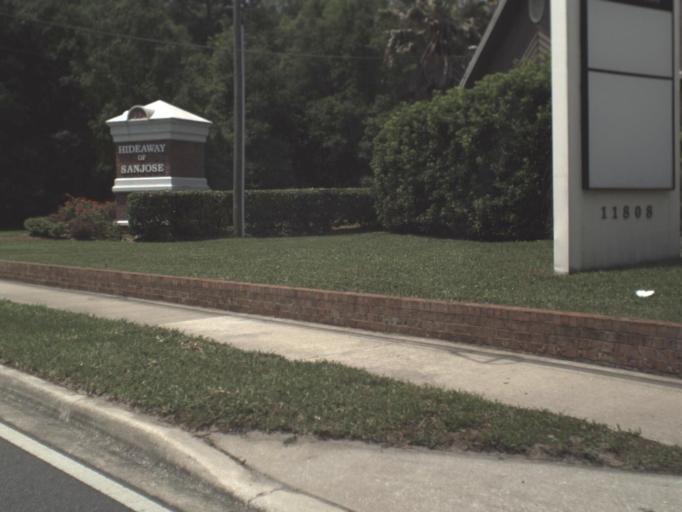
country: US
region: Florida
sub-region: Saint Johns County
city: Fruit Cove
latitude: 30.1568
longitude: -81.6328
